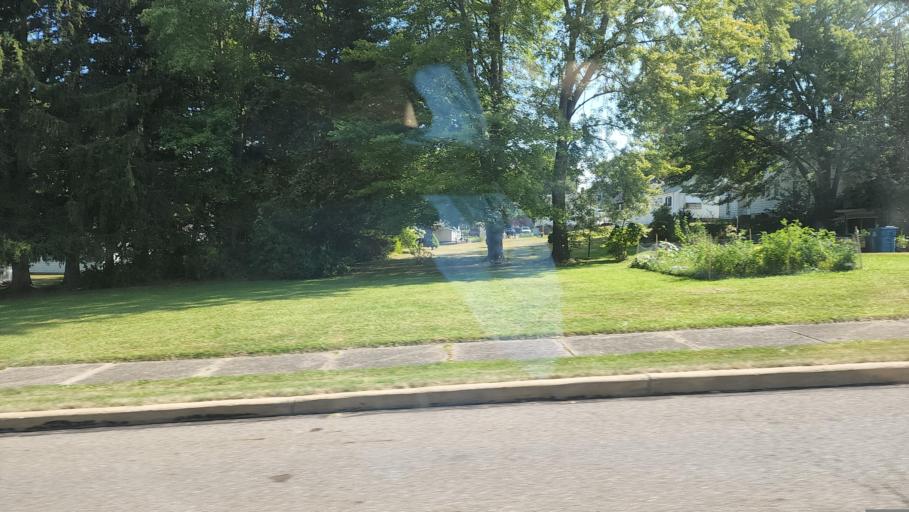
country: US
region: Ohio
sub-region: Trumbull County
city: Niles
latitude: 41.1917
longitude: -80.7519
